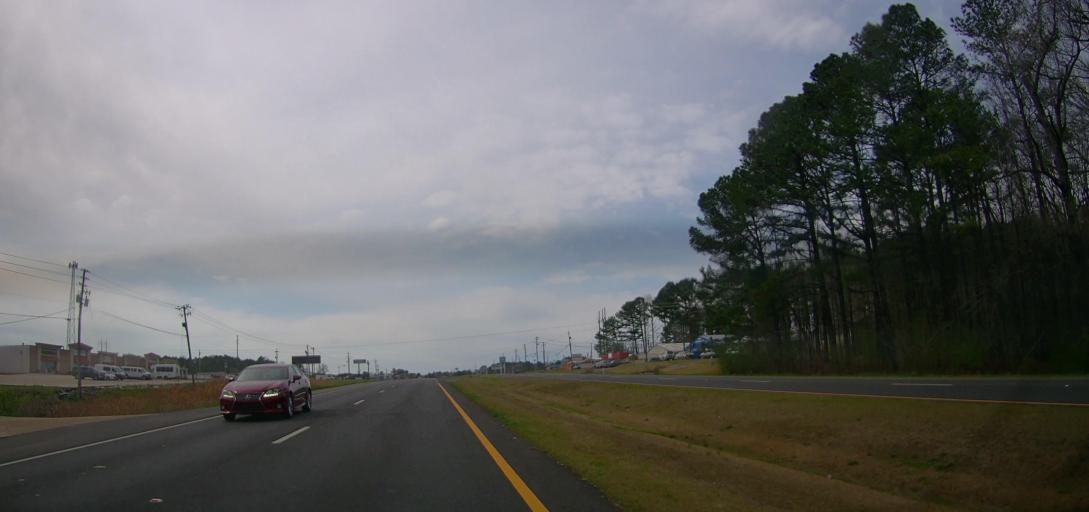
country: US
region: Alabama
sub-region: Walker County
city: Jasper
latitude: 33.8356
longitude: -87.2230
